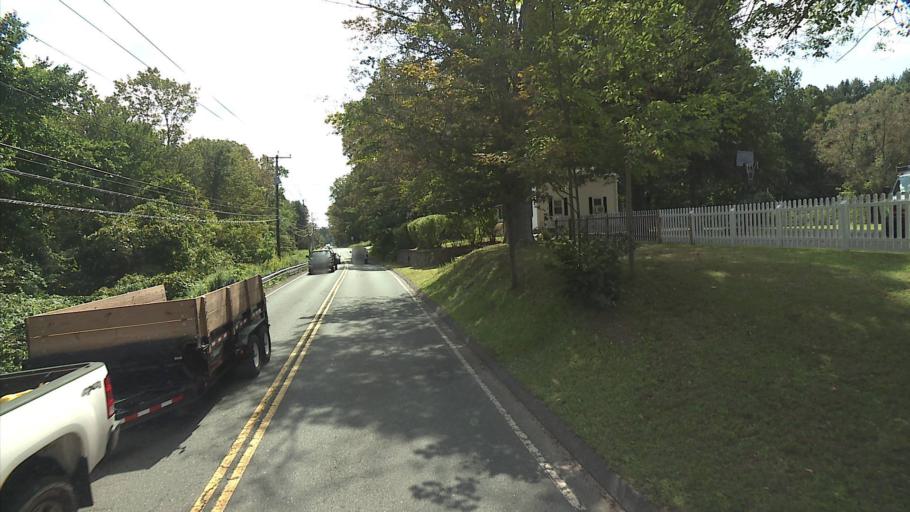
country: US
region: Connecticut
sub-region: Hartford County
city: North Granby
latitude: 41.9852
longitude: -72.8223
